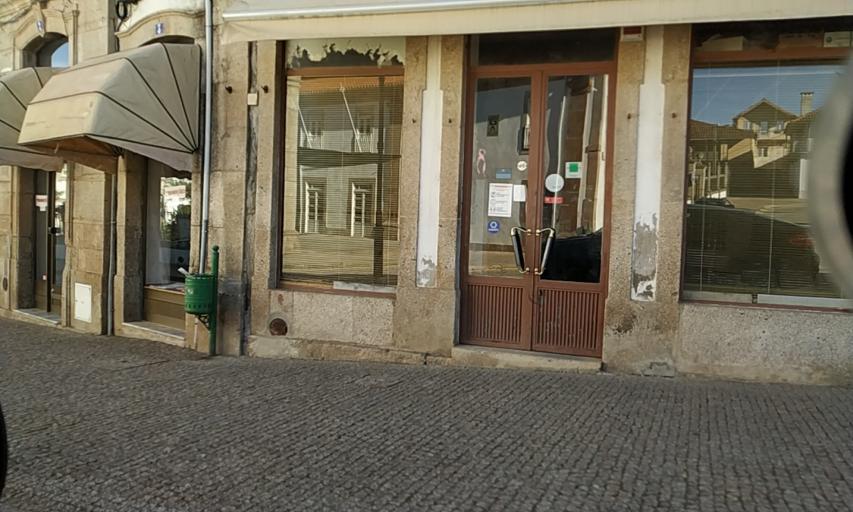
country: PT
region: Vila Real
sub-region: Murca
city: Murca
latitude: 41.4078
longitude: -7.4538
